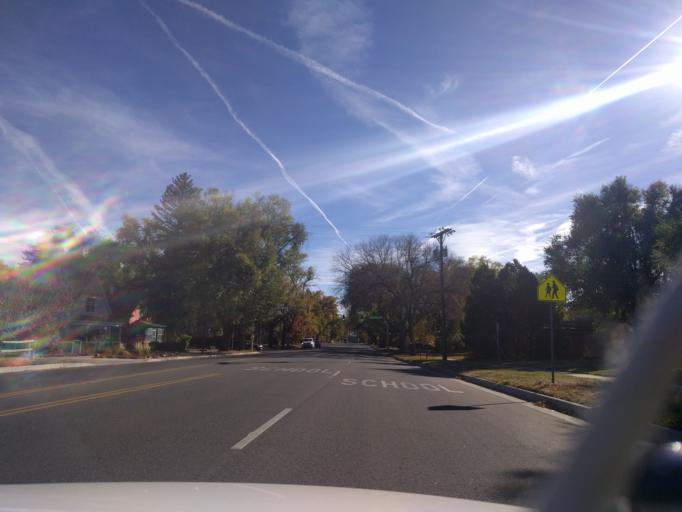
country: US
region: Colorado
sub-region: El Paso County
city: Colorado Springs
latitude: 38.8503
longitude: -104.8135
